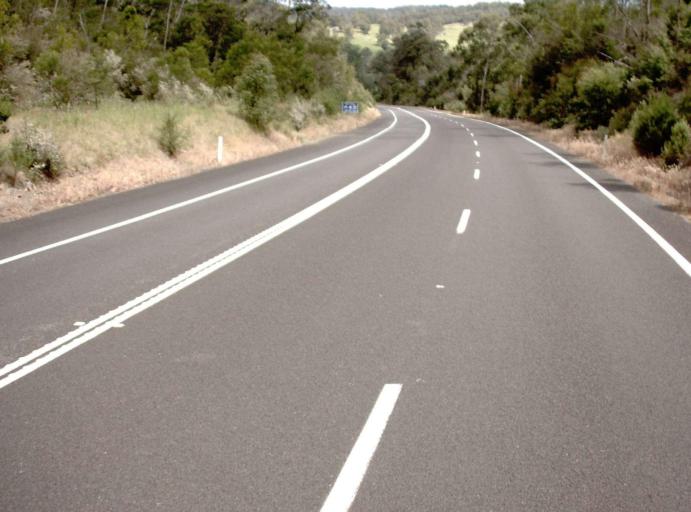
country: AU
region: New South Wales
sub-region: Bega Valley
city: Eden
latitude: -37.4657
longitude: 149.5874
